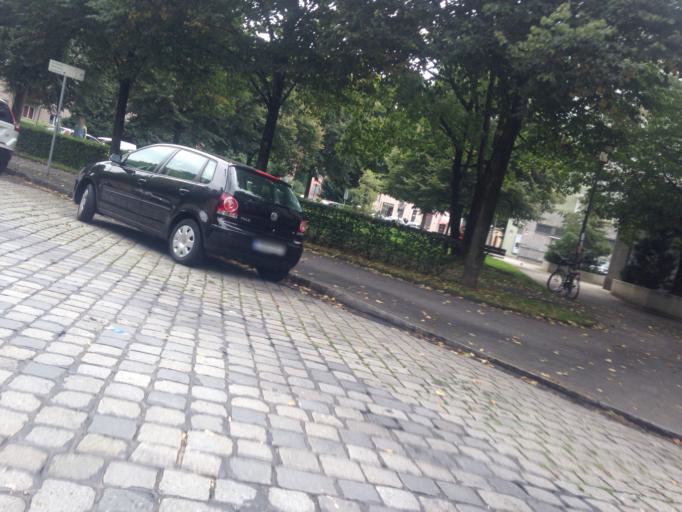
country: DE
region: Bavaria
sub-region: Upper Bavaria
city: Munich
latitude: 48.1534
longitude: 11.5681
